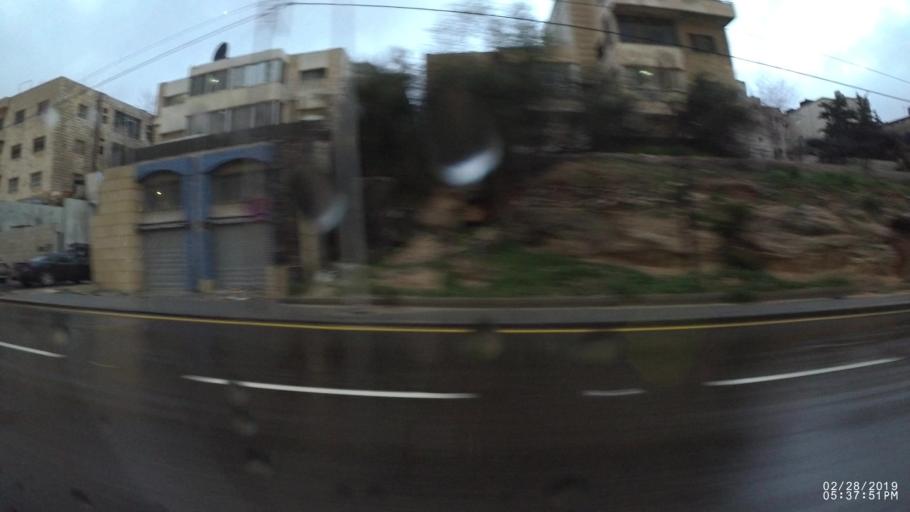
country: JO
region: Amman
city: Al Jubayhah
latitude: 31.9942
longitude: 35.8877
